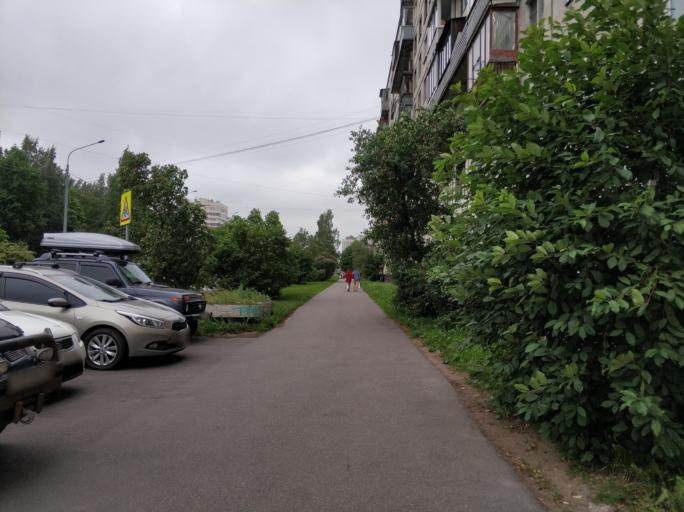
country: RU
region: St.-Petersburg
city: Grazhdanka
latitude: 60.0421
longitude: 30.4156
